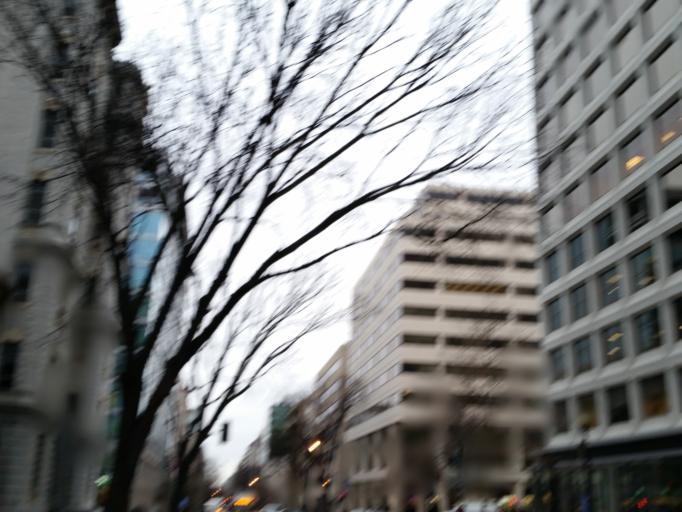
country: US
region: Washington, D.C.
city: Washington, D.C.
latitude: 38.9037
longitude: -77.0339
